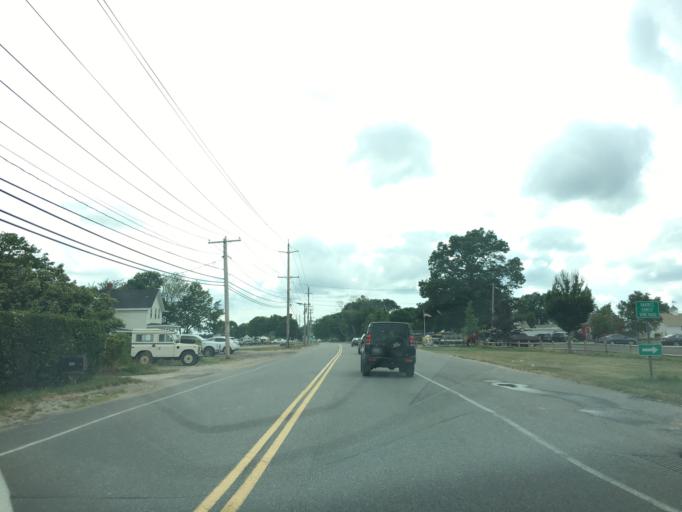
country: US
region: New York
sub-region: Suffolk County
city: Laurel
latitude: 40.9863
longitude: -72.5766
